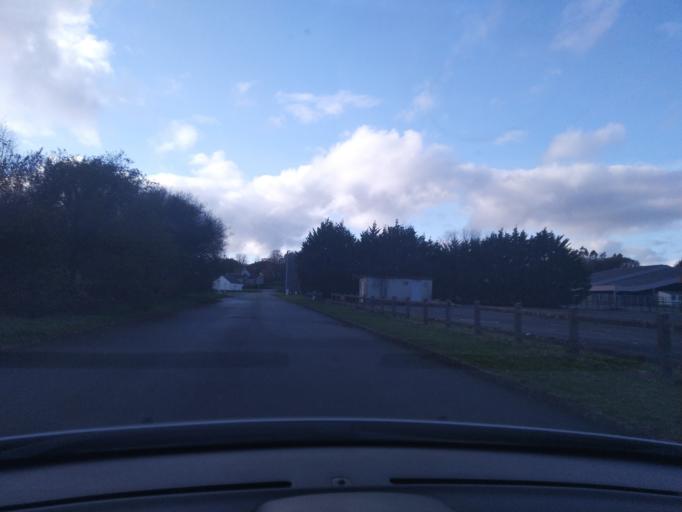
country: FR
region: Brittany
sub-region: Departement du Finistere
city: Guerlesquin
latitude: 48.5138
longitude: -3.5853
